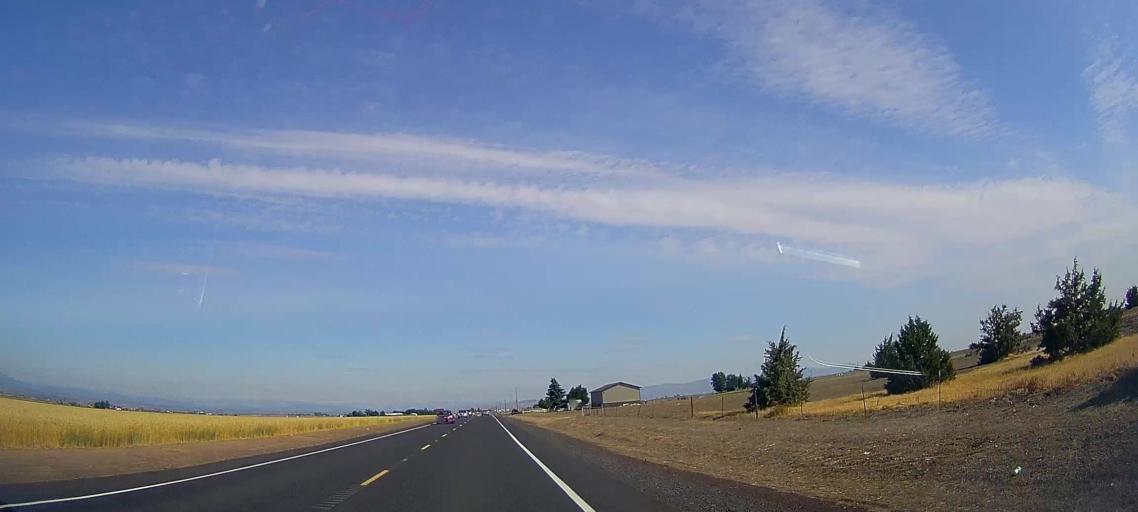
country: US
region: Oregon
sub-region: Jefferson County
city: Madras
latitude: 44.6735
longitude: -121.1422
